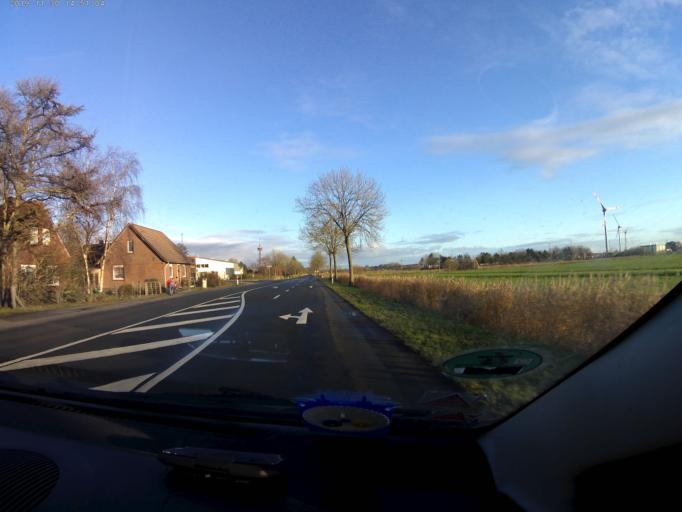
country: DE
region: Lower Saxony
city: Jemgum
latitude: 53.2618
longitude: 7.4111
